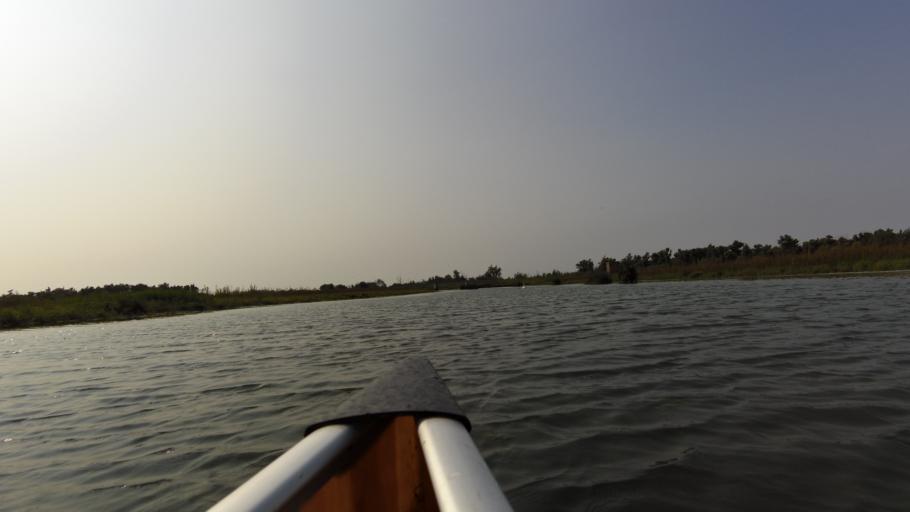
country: NL
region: South Holland
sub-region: Gemeente Sliedrecht
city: Sliedrecht
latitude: 51.7719
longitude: 4.7963
